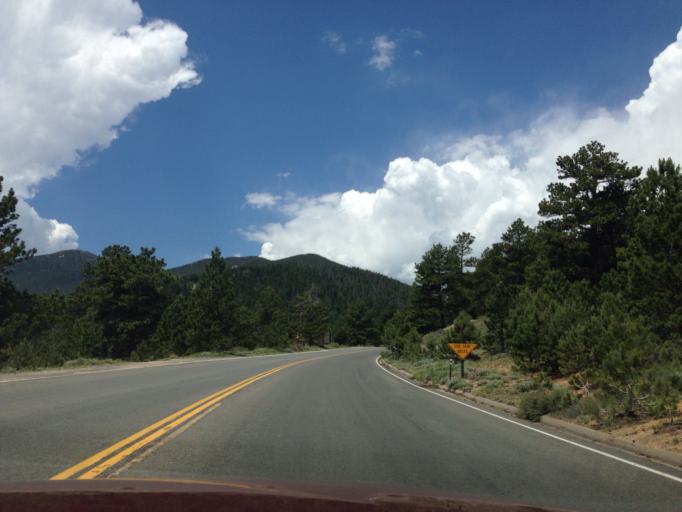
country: US
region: Colorado
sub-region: Larimer County
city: Estes Park
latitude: 40.3871
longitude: -105.6120
